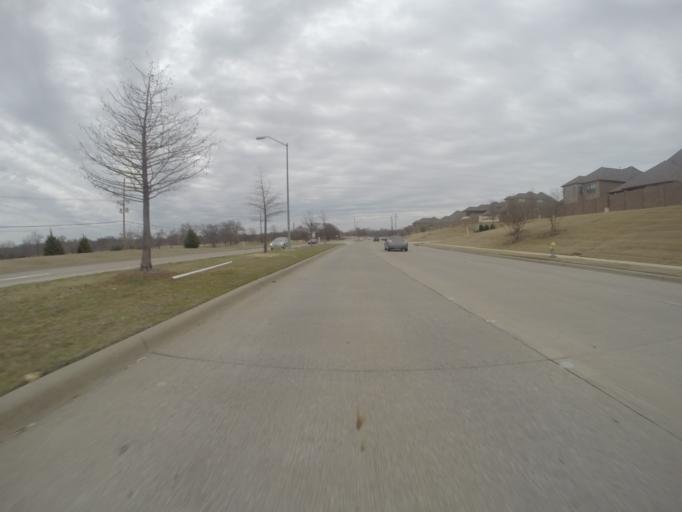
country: US
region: Texas
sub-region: Collin County
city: Saint Paul
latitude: 33.0326
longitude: -96.5627
